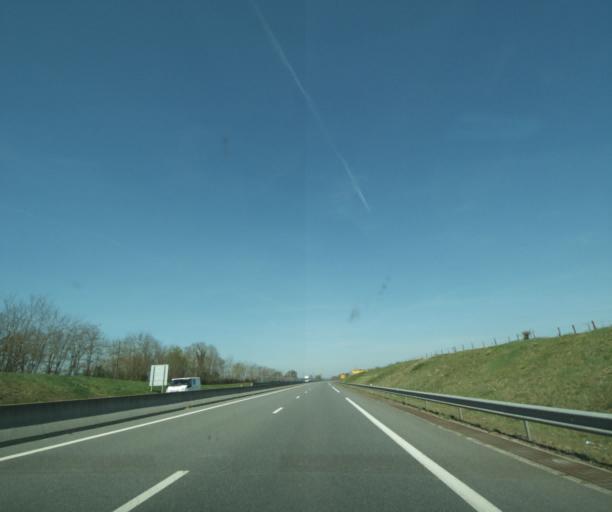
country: FR
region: Auvergne
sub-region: Departement de l'Allier
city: Trevol
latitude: 46.6095
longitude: 3.2938
